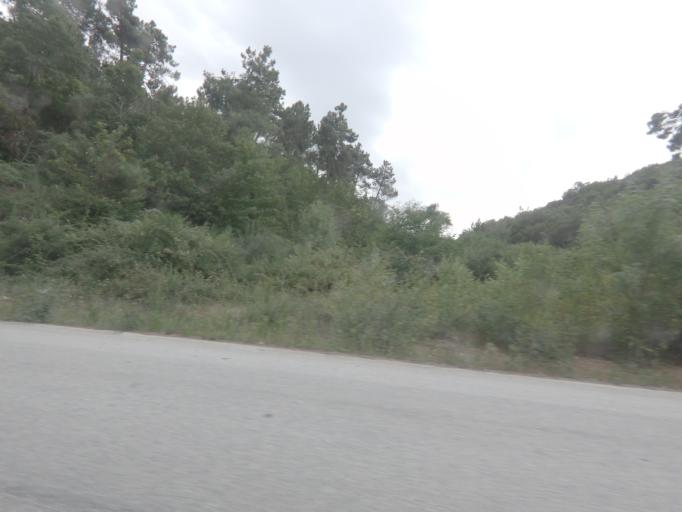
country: PT
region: Viseu
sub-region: Armamar
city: Armamar
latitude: 41.1092
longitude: -7.6784
